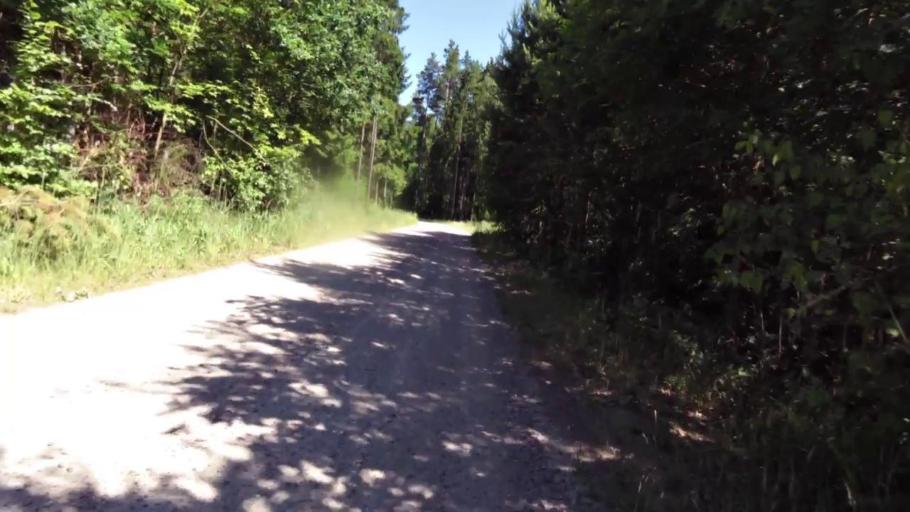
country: PL
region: West Pomeranian Voivodeship
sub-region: Powiat swidwinski
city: Rabino
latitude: 53.8842
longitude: 16.0479
